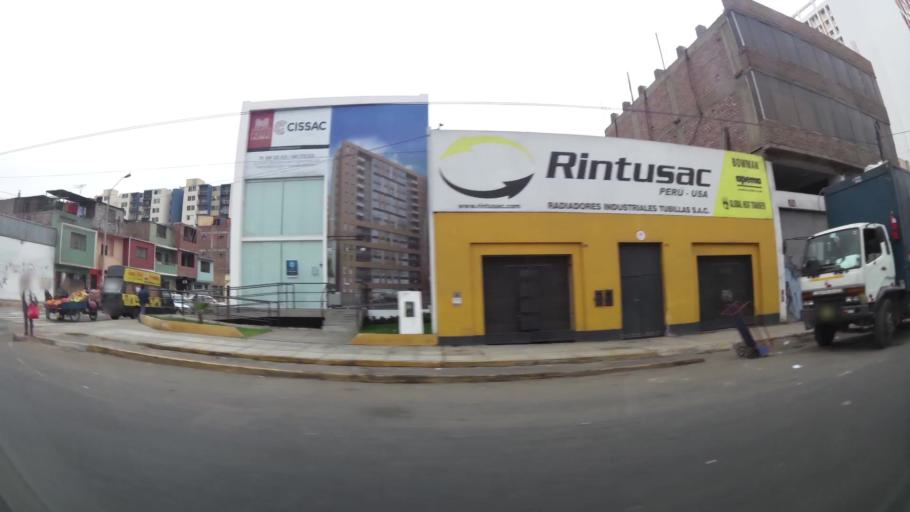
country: PE
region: Lima
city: Lima
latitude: -12.0471
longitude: -77.0494
